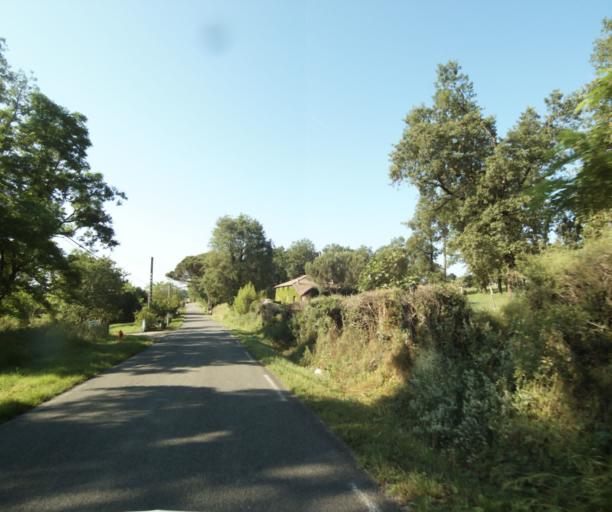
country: FR
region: Midi-Pyrenees
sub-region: Departement du Tarn-et-Garonne
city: Saint-Etienne-de-Tulmont
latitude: 44.0179
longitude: 1.4305
